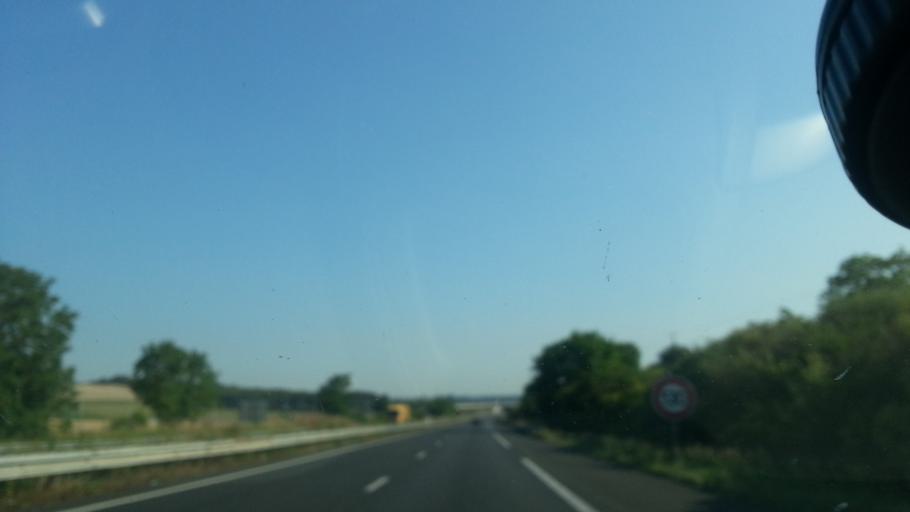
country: FR
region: Poitou-Charentes
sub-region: Departement de la Vienne
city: Les Ormes
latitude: 46.9947
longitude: 0.5505
